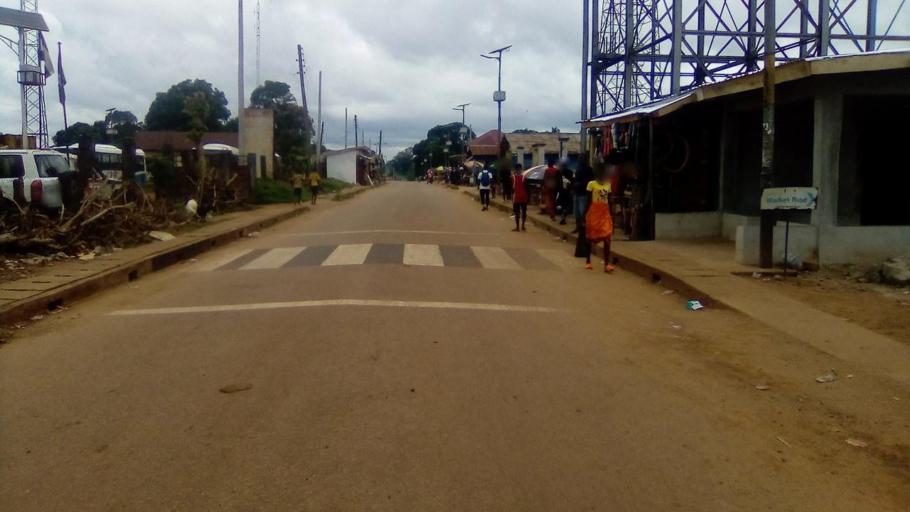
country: SL
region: Southern Province
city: Pujehun
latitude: 7.3573
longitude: -11.7218
